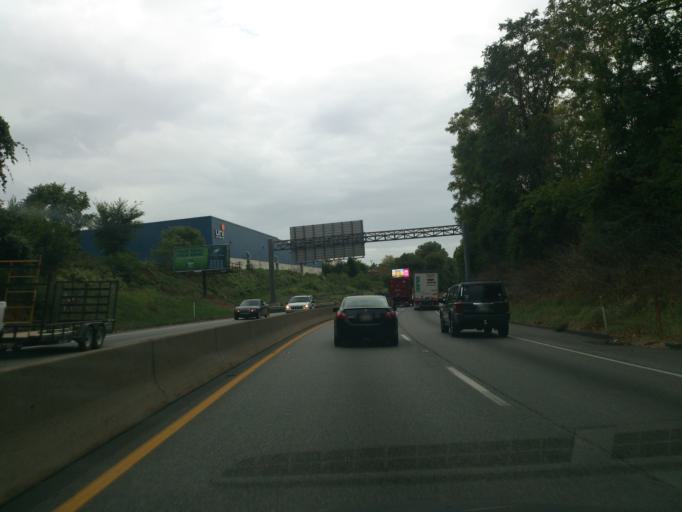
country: US
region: Pennsylvania
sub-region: Berks County
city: Reading
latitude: 40.3198
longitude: -75.9234
